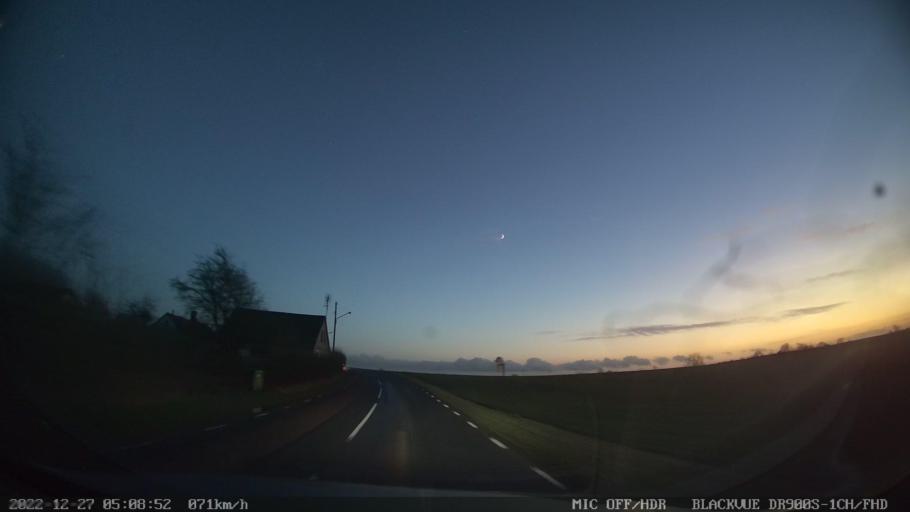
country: SE
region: Skane
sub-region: Simrishamns Kommun
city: Kivik
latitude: 55.5667
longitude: 14.1547
